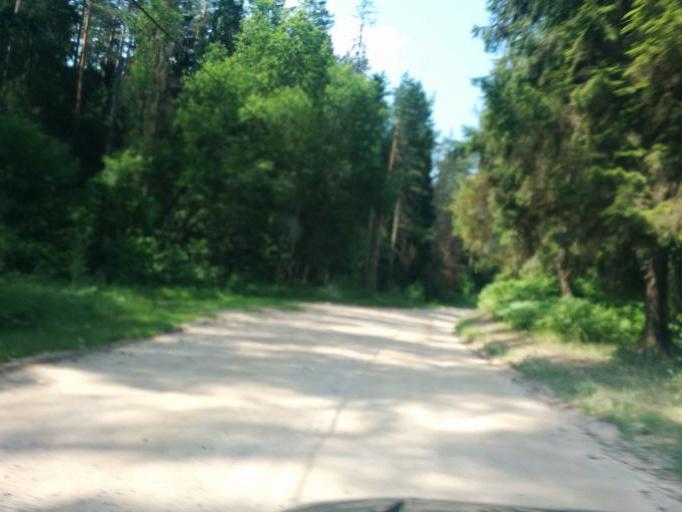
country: LV
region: Baldone
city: Baldone
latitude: 56.7429
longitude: 24.4347
